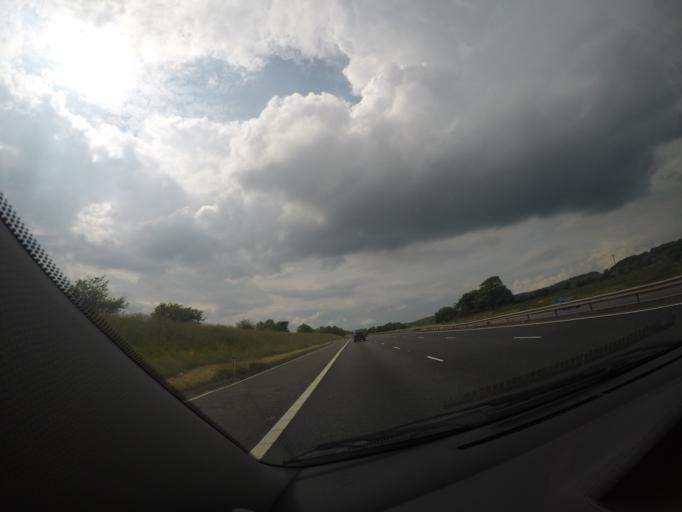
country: GB
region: Scotland
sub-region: Dumfries and Galloway
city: Lockerbie
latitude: 55.0699
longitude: -3.2907
